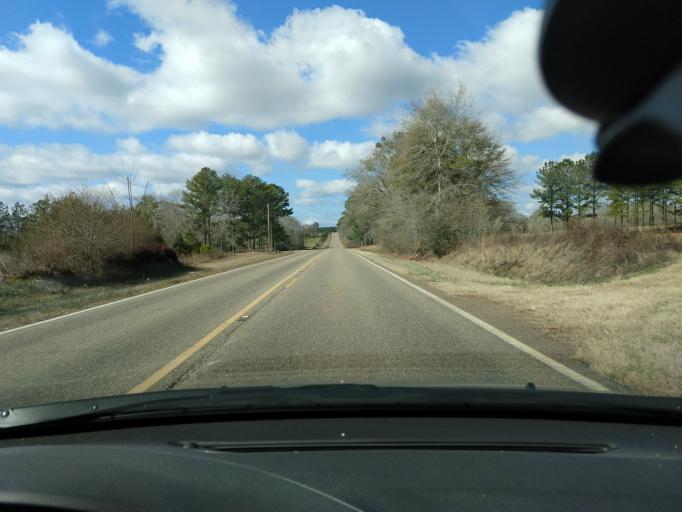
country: US
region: Alabama
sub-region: Coffee County
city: Elba
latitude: 31.3117
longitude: -86.0208
